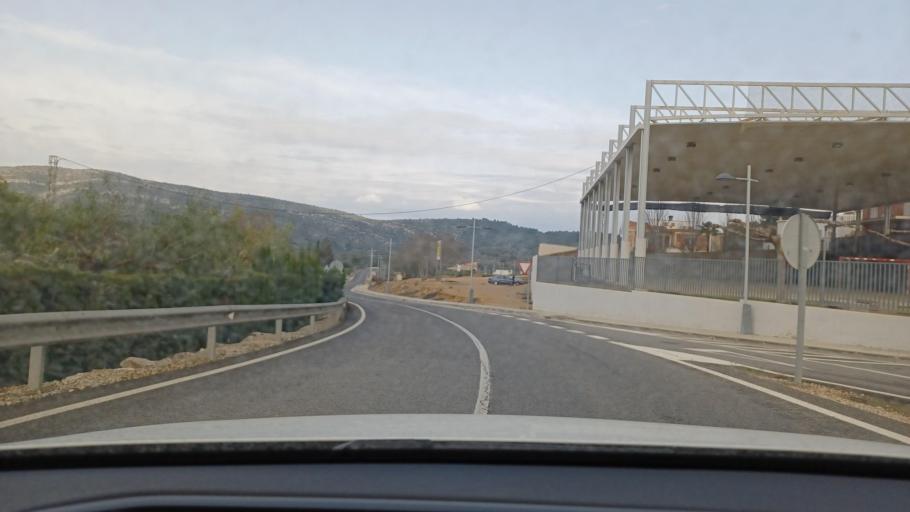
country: ES
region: Catalonia
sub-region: Provincia de Tarragona
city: Masdenverge
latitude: 40.6696
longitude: 0.5206
